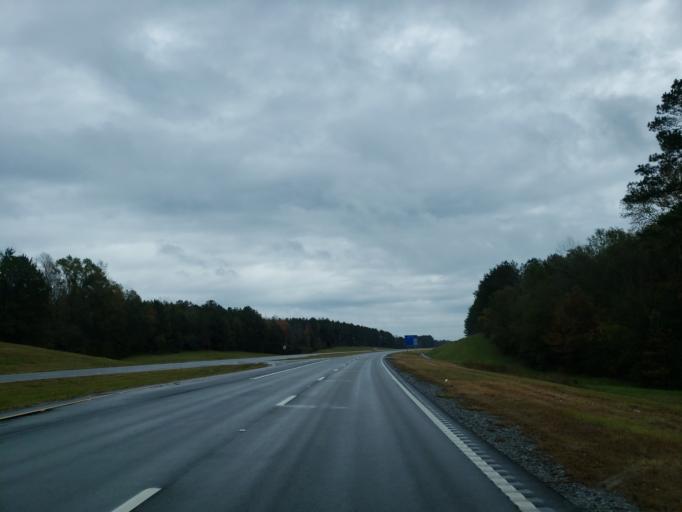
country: US
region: Mississippi
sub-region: Wayne County
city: Waynesboro
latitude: 31.7007
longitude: -88.6547
